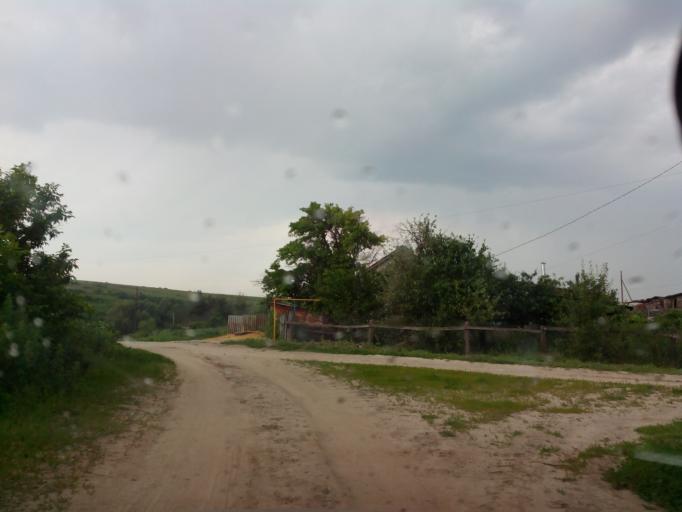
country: RU
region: Volgograd
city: Slashchevskaya
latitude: 49.7780
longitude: 42.4580
